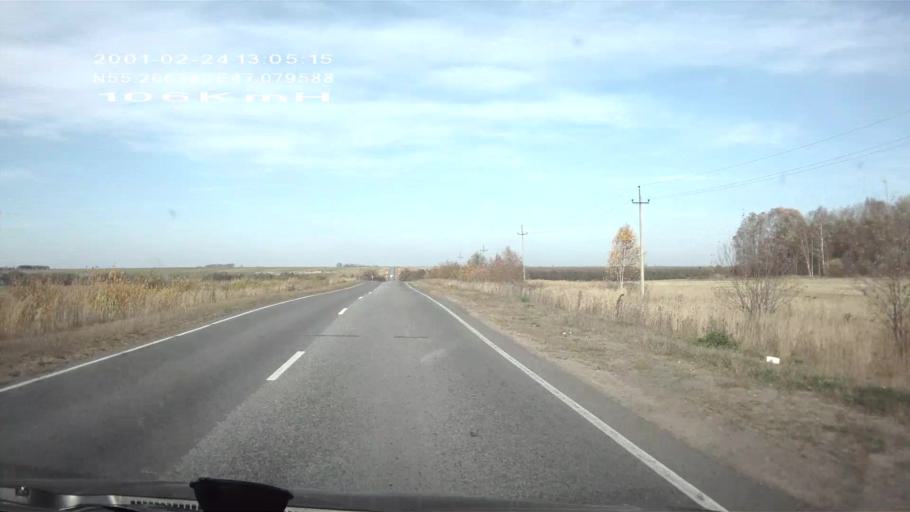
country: RU
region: Chuvashia
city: Ibresi
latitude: 55.2664
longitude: 47.0796
